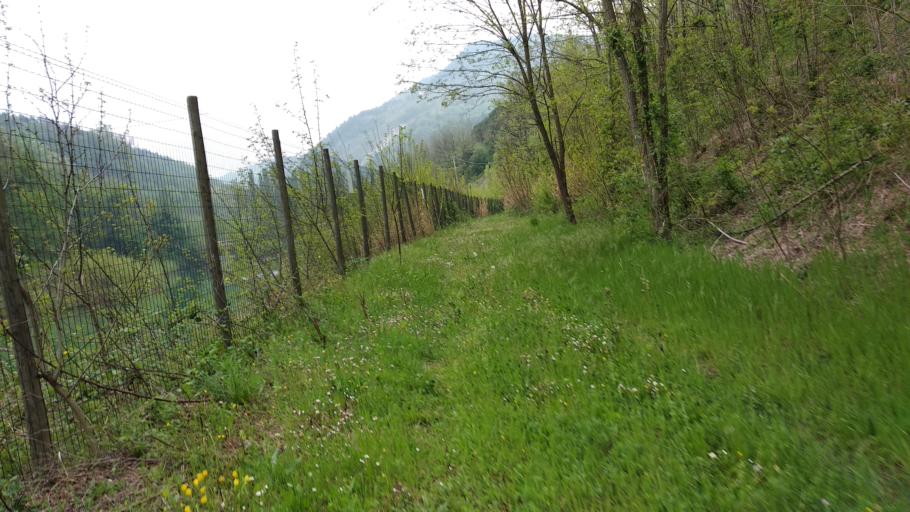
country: IT
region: Emilia-Romagna
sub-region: Forli-Cesena
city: Modigliana
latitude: 44.1403
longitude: 11.8009
